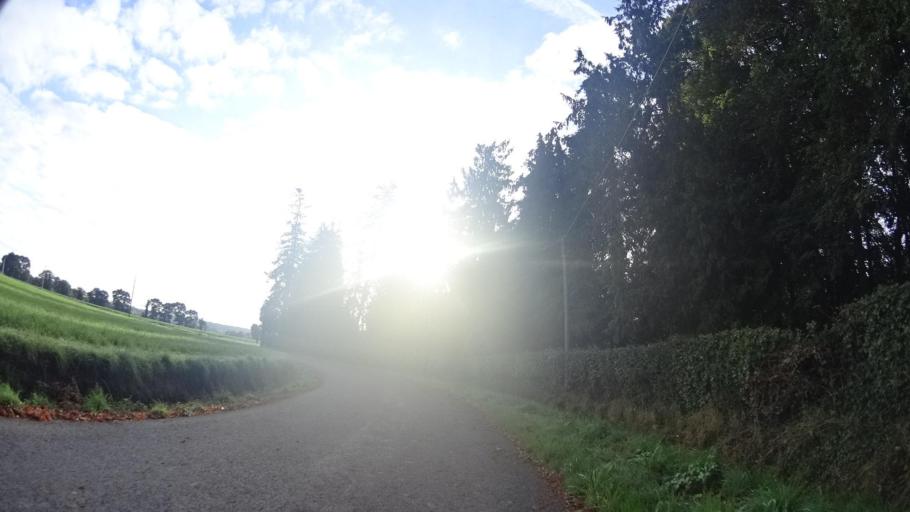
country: FR
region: Brittany
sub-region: Departement des Cotes-d'Armor
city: Evran
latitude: 48.3570
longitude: -1.9473
